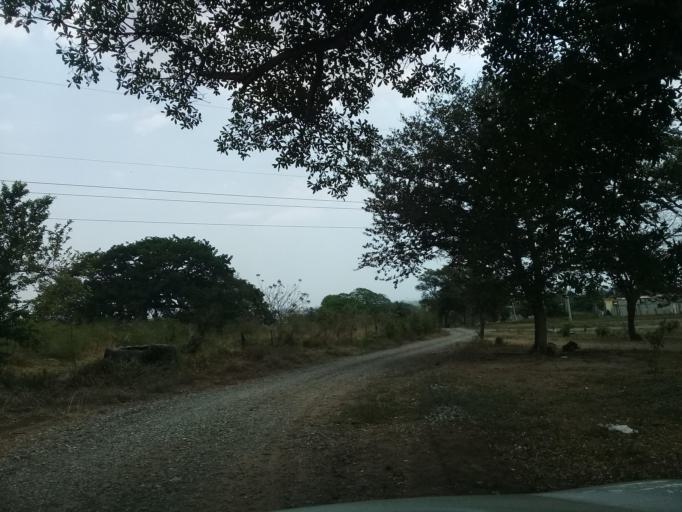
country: MX
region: Veracruz
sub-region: Veracruz
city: Las Amapolas
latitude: 19.1404
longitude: -96.2401
